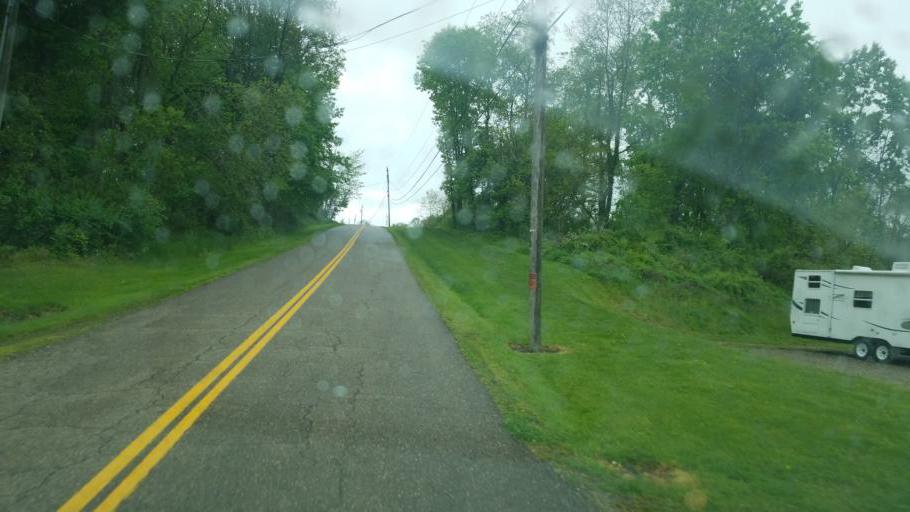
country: US
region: Ohio
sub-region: Jefferson County
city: Tiltonsville
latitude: 40.2146
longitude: -80.6965
